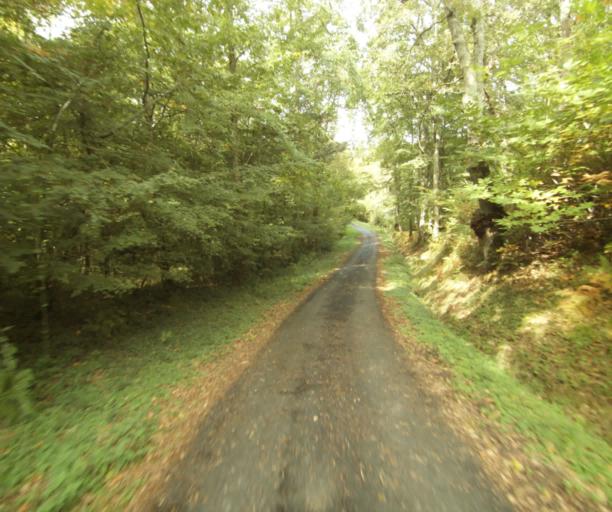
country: FR
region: Midi-Pyrenees
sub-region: Departement du Gers
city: Eauze
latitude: 43.8317
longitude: 0.1005
